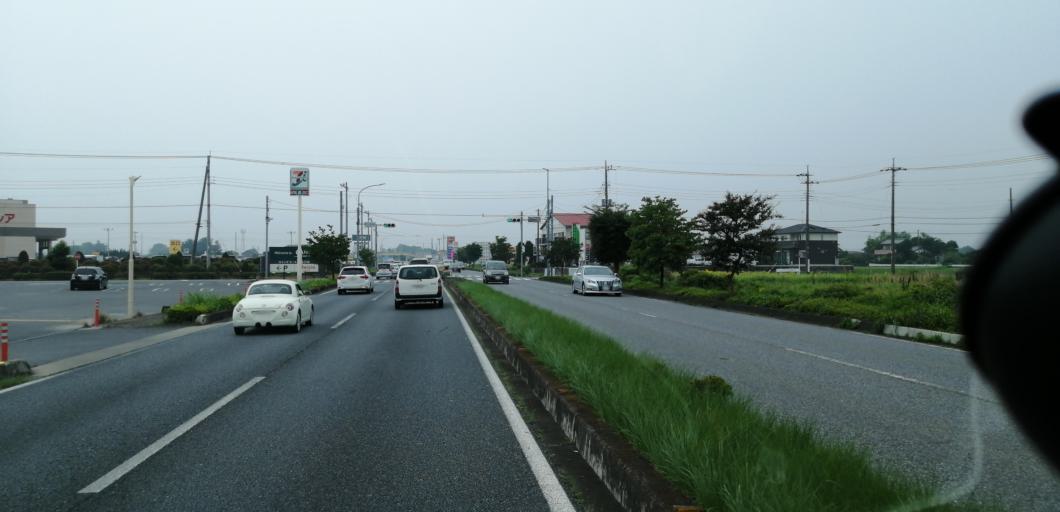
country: JP
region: Saitama
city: Fukayacho
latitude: 36.1505
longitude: 139.2963
